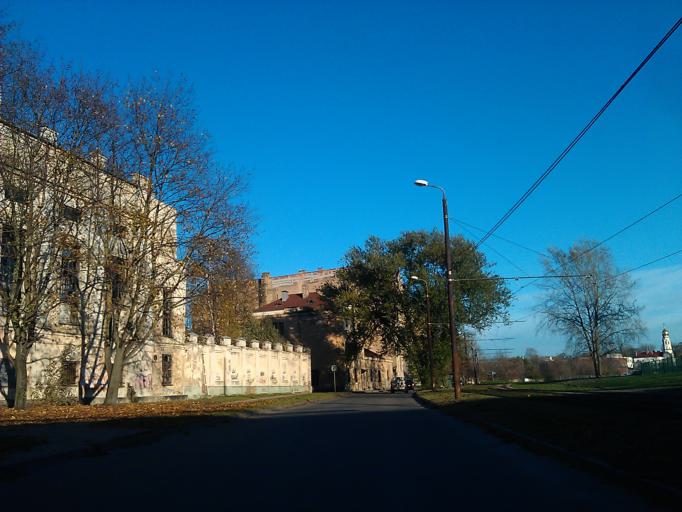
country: LV
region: Riga
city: Riga
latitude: 56.9389
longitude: 24.1302
